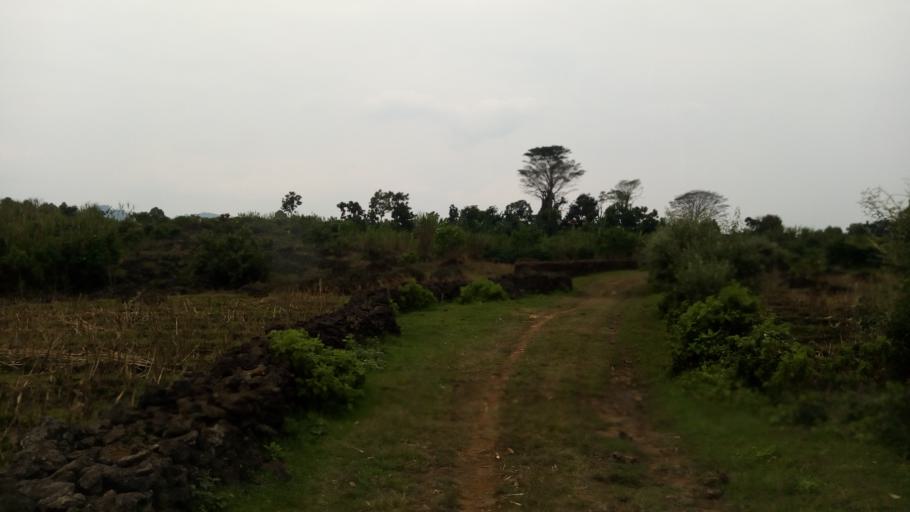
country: UG
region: Western Region
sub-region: Kisoro District
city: Kisoro
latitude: -1.2653
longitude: 29.6081
